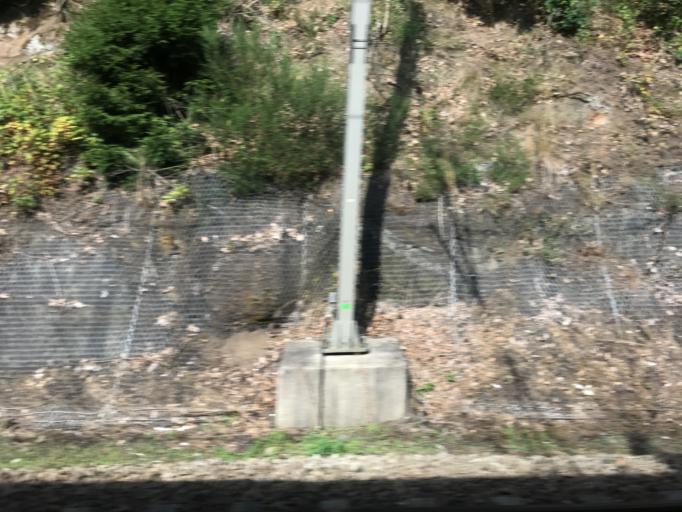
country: CZ
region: Central Bohemia
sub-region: Okres Benesov
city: Cercany
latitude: 49.8255
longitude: 14.7036
